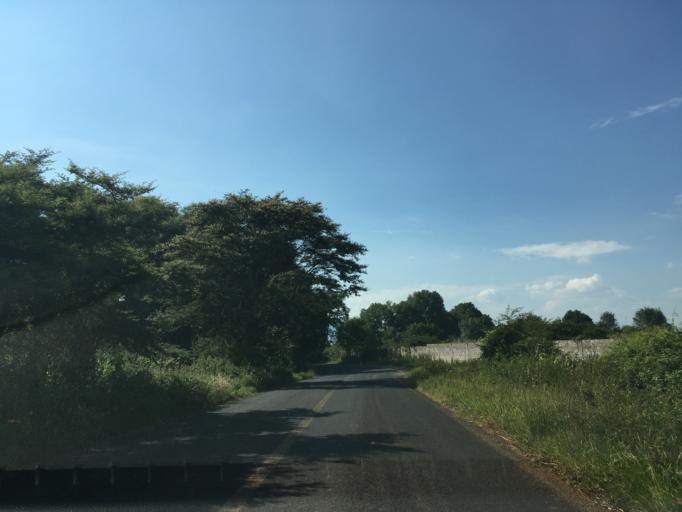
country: MX
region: Michoacan
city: Acuitzio del Canje
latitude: 19.5535
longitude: -101.2661
